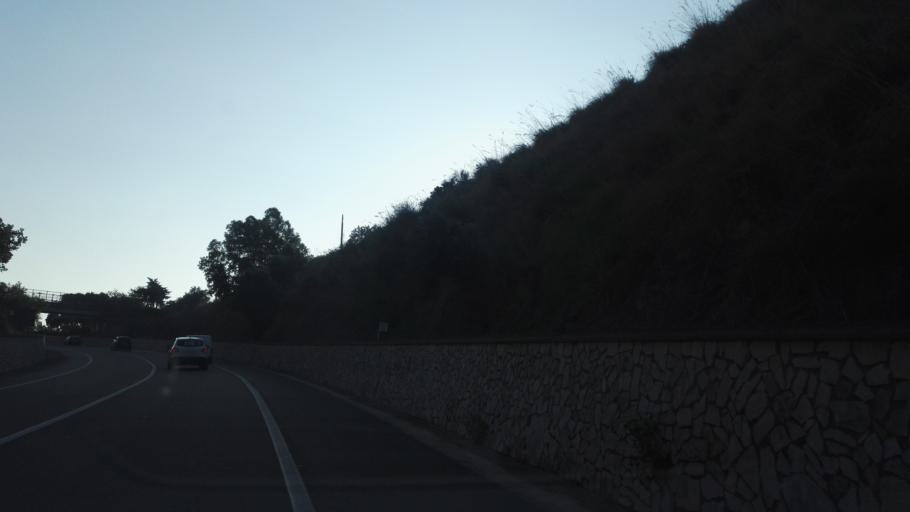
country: IT
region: Calabria
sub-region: Provincia di Catanzaro
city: Montepaone Lido
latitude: 38.7447
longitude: 16.5539
